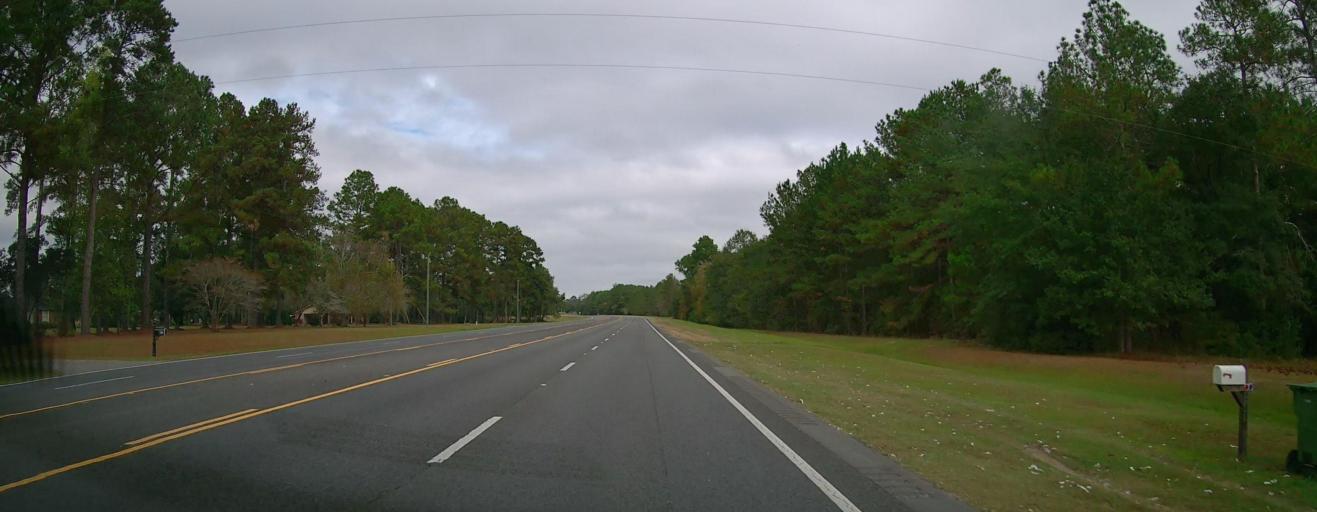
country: US
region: Georgia
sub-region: Colquitt County
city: Moultrie
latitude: 31.0584
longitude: -83.8316
